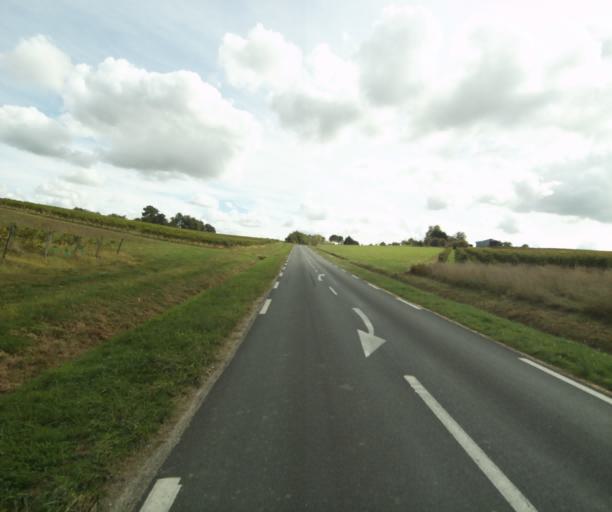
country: FR
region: Midi-Pyrenees
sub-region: Departement du Gers
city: Eauze
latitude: 43.8284
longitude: 0.0930
